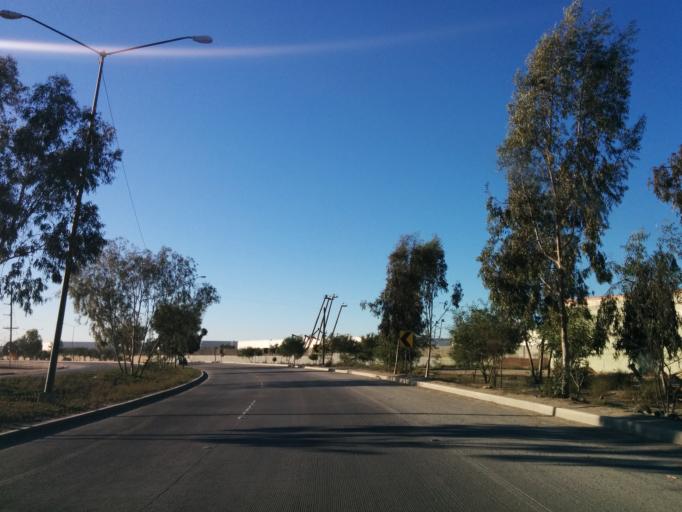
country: MX
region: Baja California
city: Tijuana
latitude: 32.5486
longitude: -116.9497
